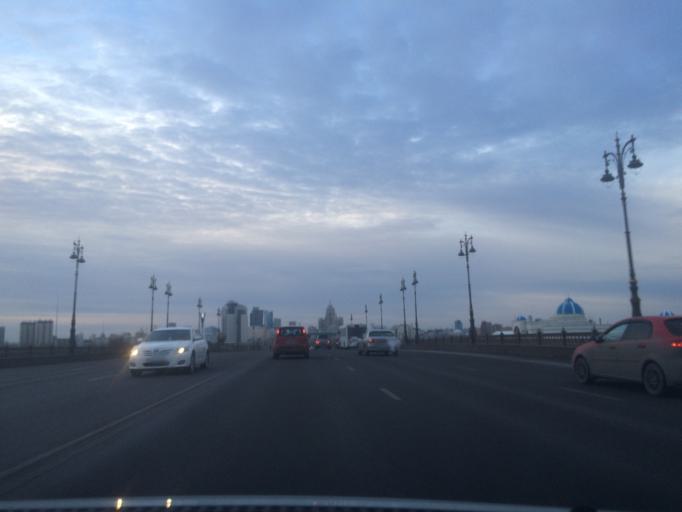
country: KZ
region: Astana Qalasy
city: Astana
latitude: 51.1582
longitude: 71.4111
